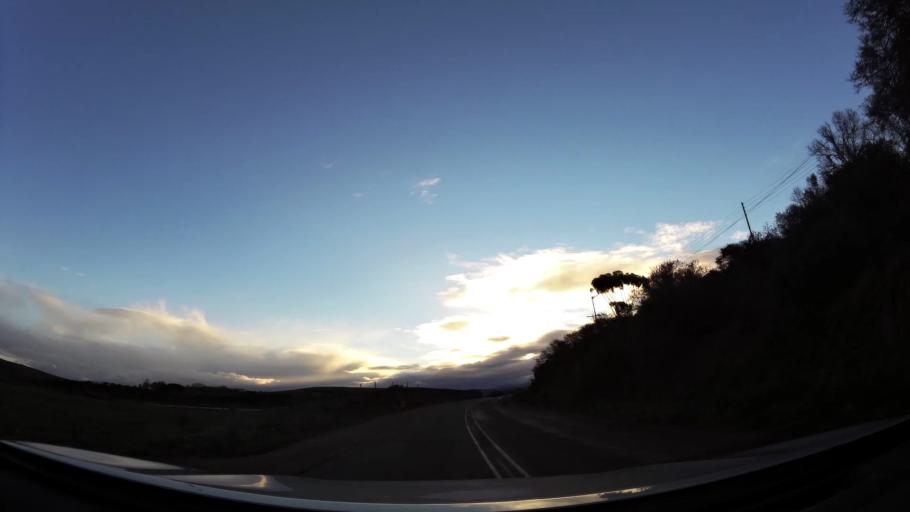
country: ZA
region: Western Cape
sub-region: Eden District Municipality
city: Riversdale
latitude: -34.0742
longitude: 20.9120
